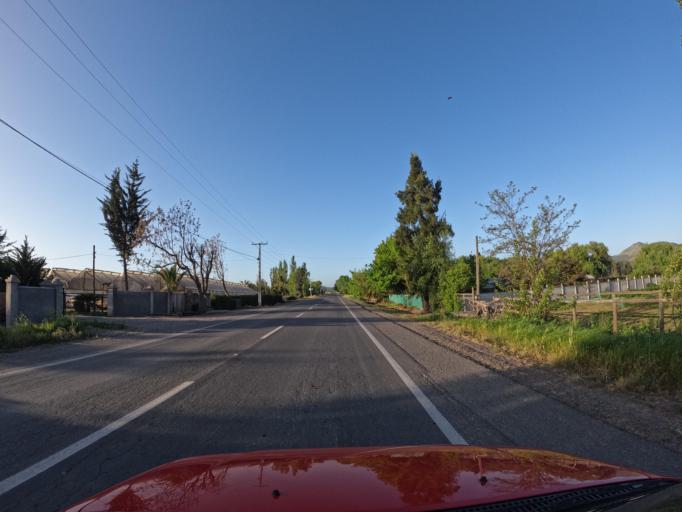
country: CL
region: O'Higgins
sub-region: Provincia de Colchagua
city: Santa Cruz
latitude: -34.3691
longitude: -71.4152
